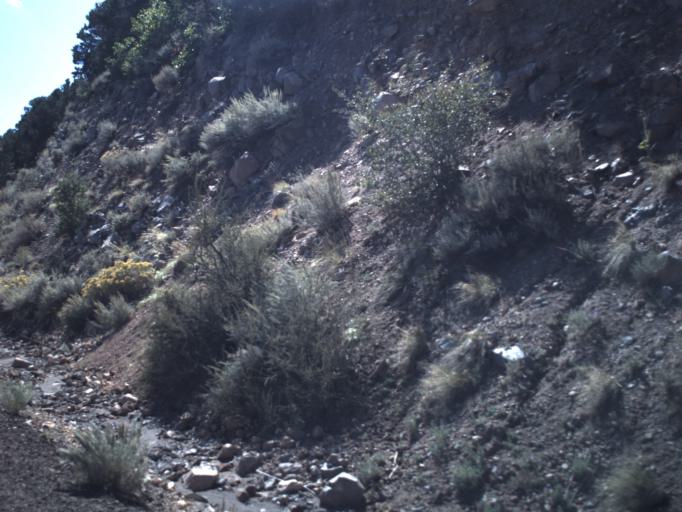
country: US
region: Utah
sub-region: Piute County
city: Junction
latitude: 38.2535
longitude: -112.3079
